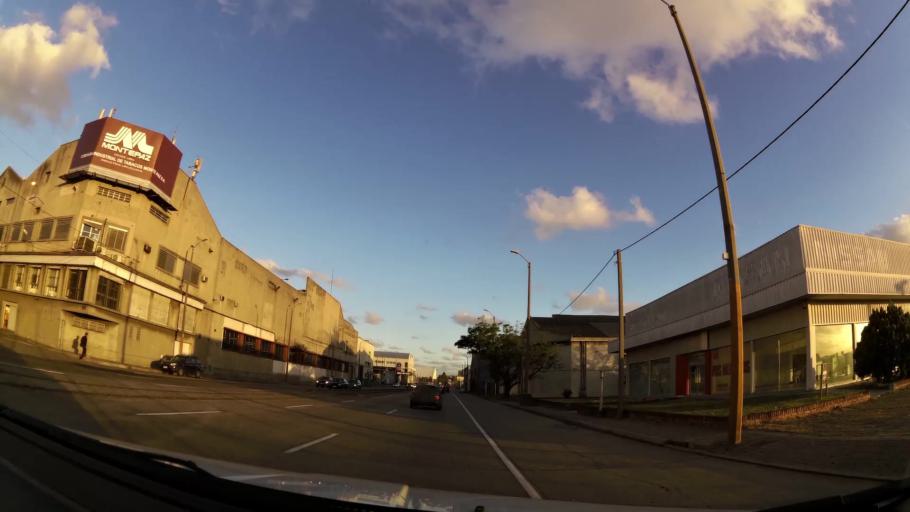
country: UY
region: Montevideo
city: Montevideo
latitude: -34.8769
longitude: -56.2084
